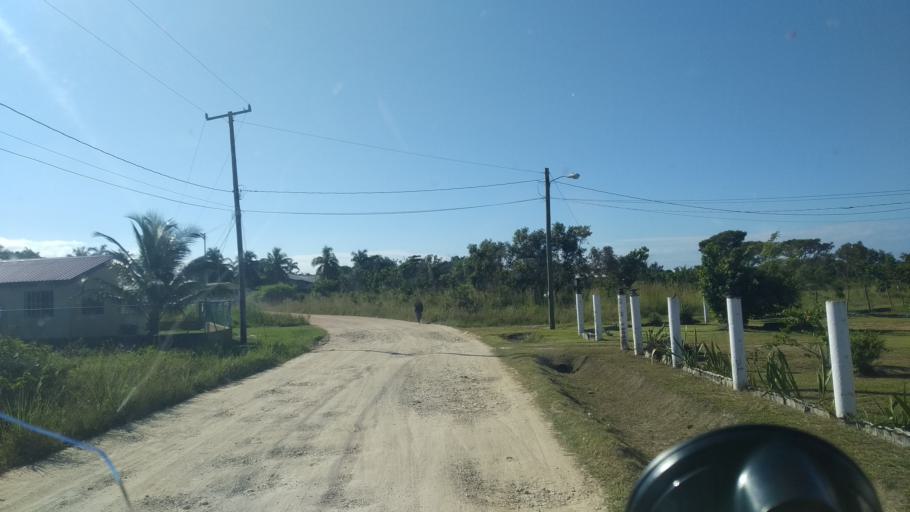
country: BZ
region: Belize
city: Belize City
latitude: 17.5522
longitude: -88.3262
